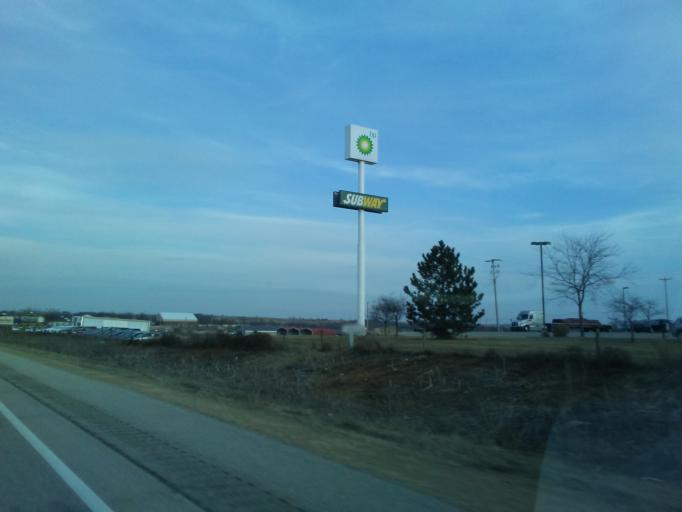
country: US
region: Wisconsin
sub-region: Iowa County
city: Barneveld
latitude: 43.0096
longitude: -89.9018
